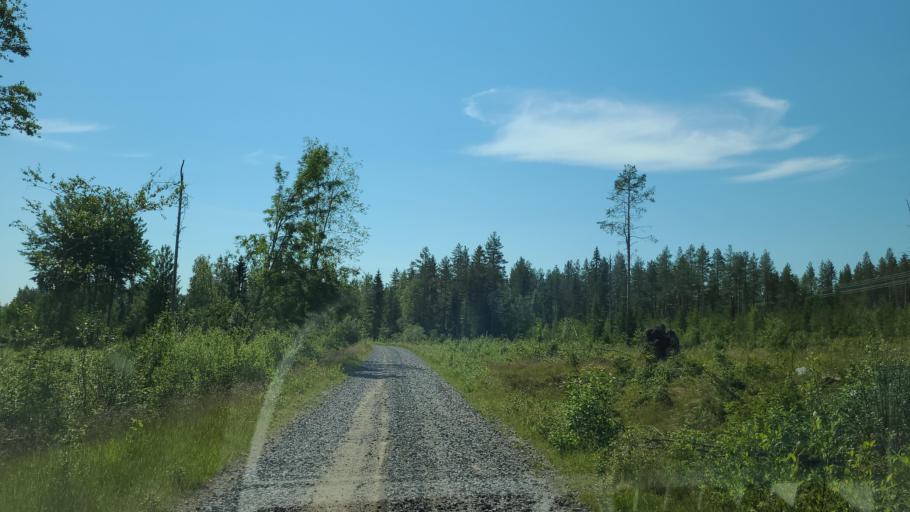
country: SE
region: Vaesterbotten
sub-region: Robertsfors Kommun
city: Robertsfors
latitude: 64.0925
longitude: 20.8355
